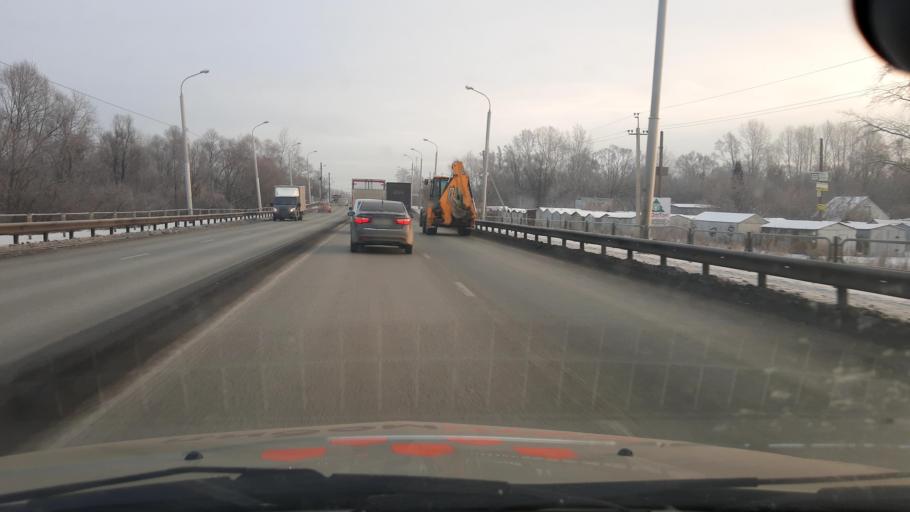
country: RU
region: Bashkortostan
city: Ufa
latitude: 54.8039
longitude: 56.1466
